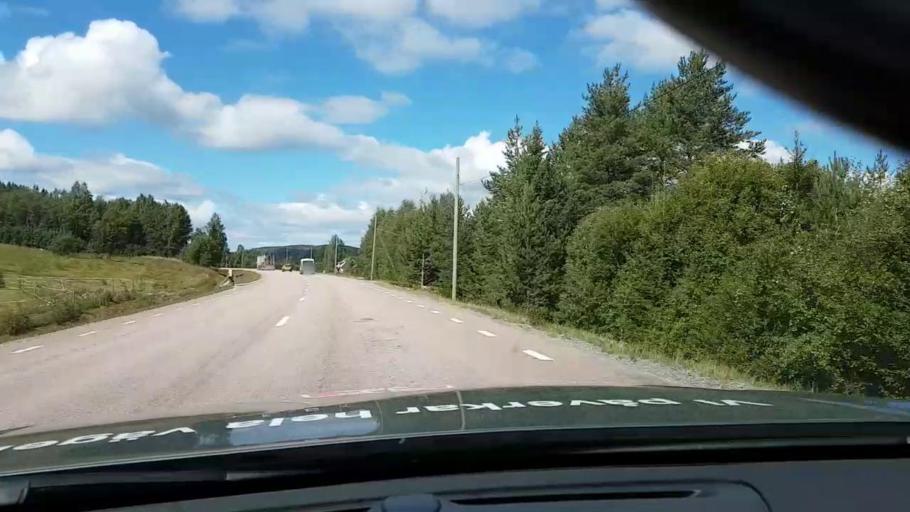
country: SE
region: Vaesternorrland
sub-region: OErnskoeldsviks Kommun
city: Bjasta
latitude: 63.3560
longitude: 18.4841
